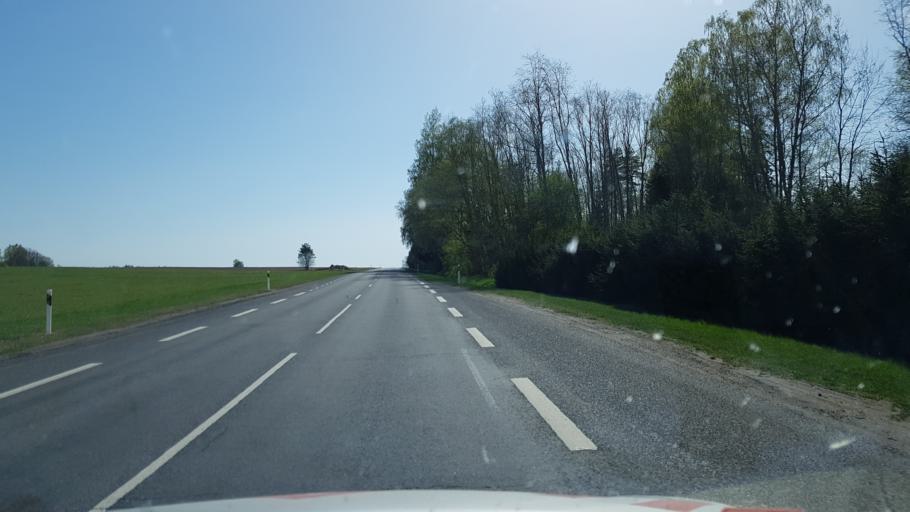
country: EE
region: Viljandimaa
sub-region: Viljandi linn
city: Viljandi
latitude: 58.3211
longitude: 25.5712
